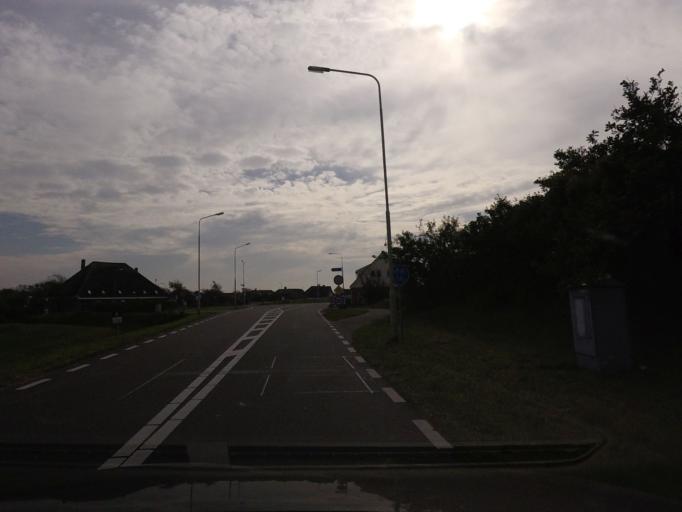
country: NL
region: North Holland
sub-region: Gemeente Den Helder
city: Den Helder
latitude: 52.8641
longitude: 4.7133
